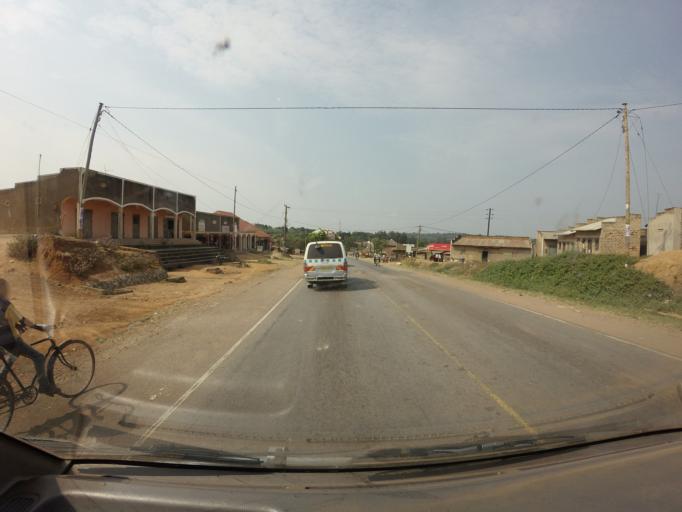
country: UG
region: Central Region
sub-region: Lwengo District
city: Lwengo
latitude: -0.3978
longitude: 31.4072
